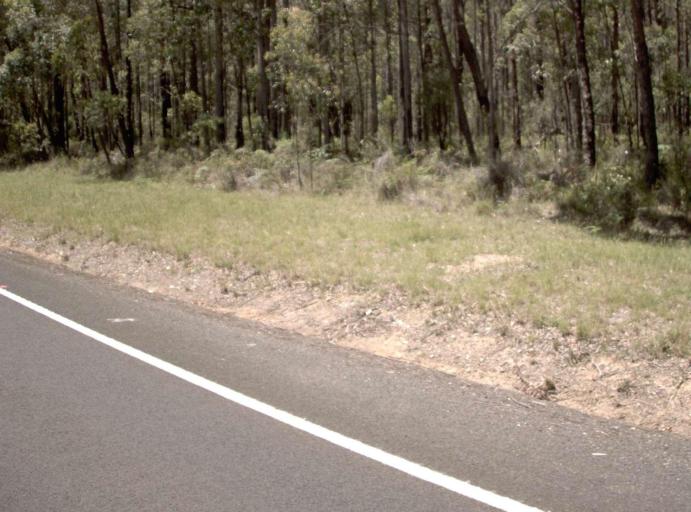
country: AU
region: Victoria
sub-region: East Gippsland
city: Lakes Entrance
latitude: -37.6972
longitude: 148.5888
